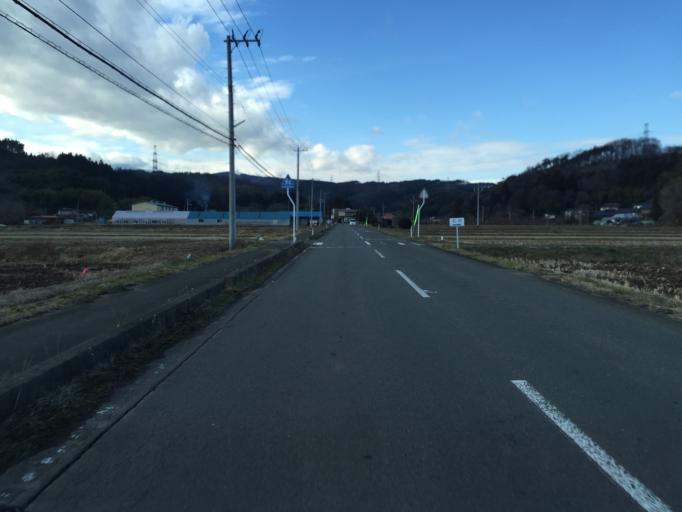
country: JP
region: Fukushima
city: Nihommatsu
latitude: 37.6664
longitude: 140.4211
